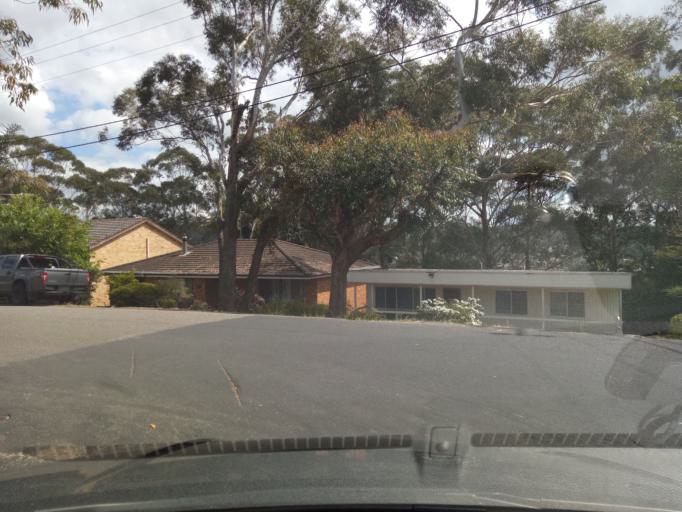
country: AU
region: New South Wales
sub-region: Gosford Shire
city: Narara
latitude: -33.3937
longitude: 151.3551
